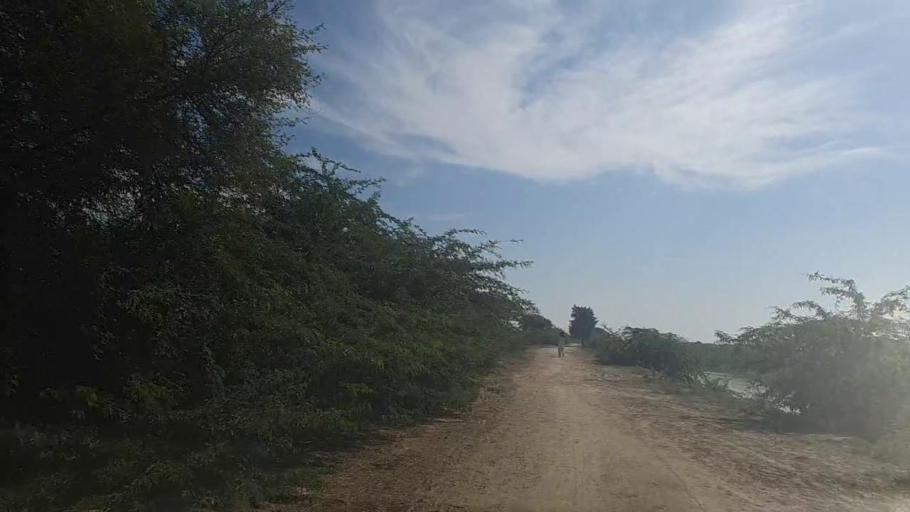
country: PK
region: Sindh
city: Mirpur Batoro
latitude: 24.6620
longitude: 68.1908
